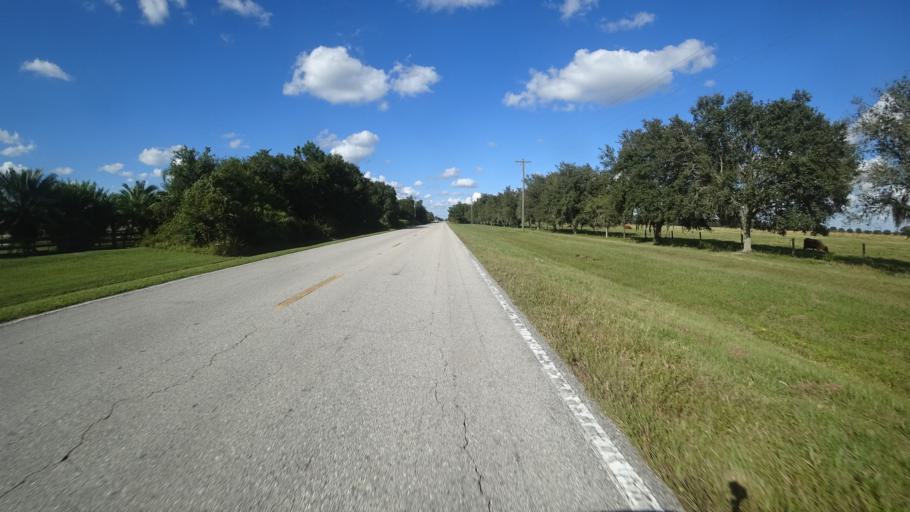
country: US
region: Florida
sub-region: Sarasota County
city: The Meadows
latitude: 27.4202
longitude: -82.3037
